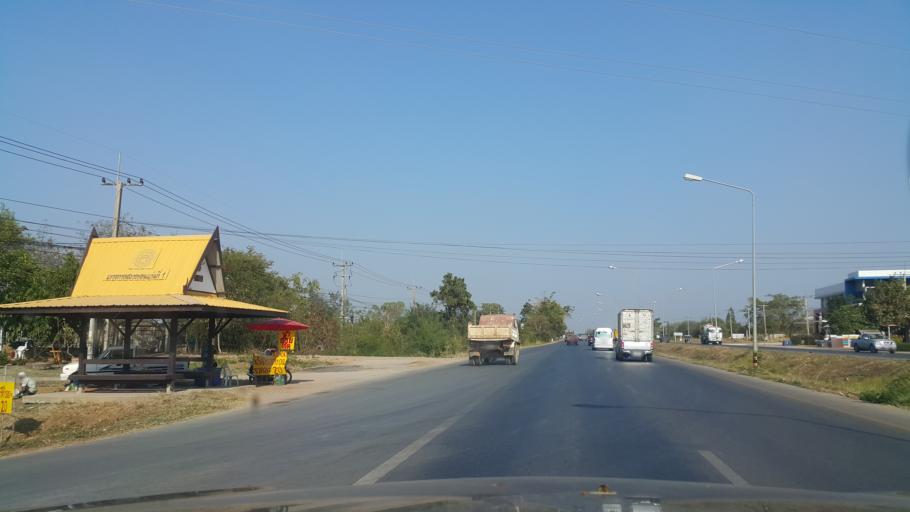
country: TH
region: Khon Kaen
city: Khon Kaen
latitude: 16.3999
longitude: 102.8687
